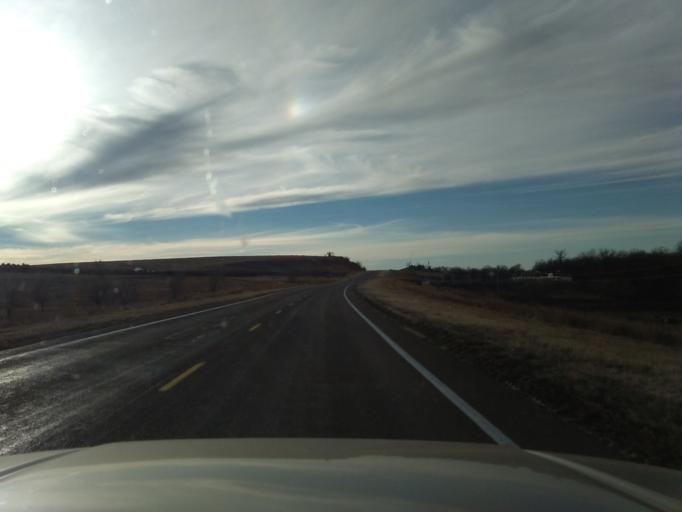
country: US
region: Kansas
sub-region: Norton County
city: Norton
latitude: 39.7215
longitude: -100.1944
